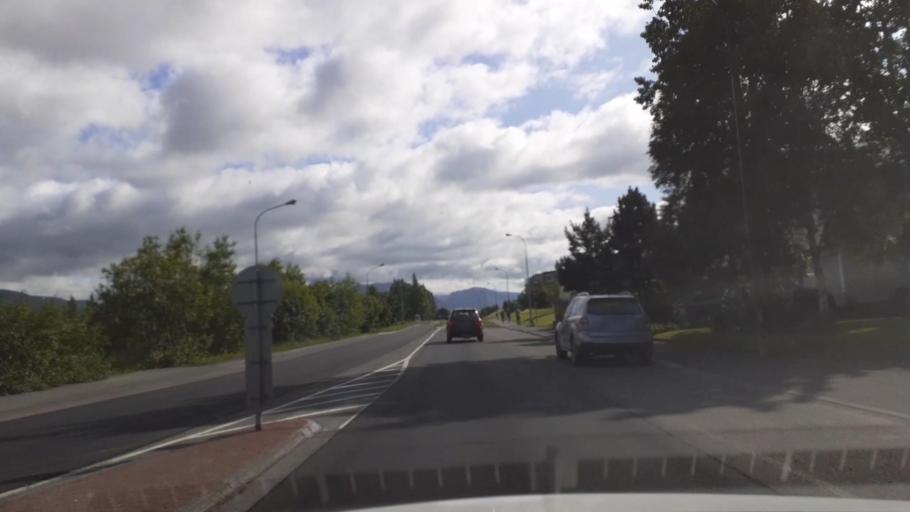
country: IS
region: Northeast
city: Akureyri
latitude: 65.6757
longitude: -18.0979
